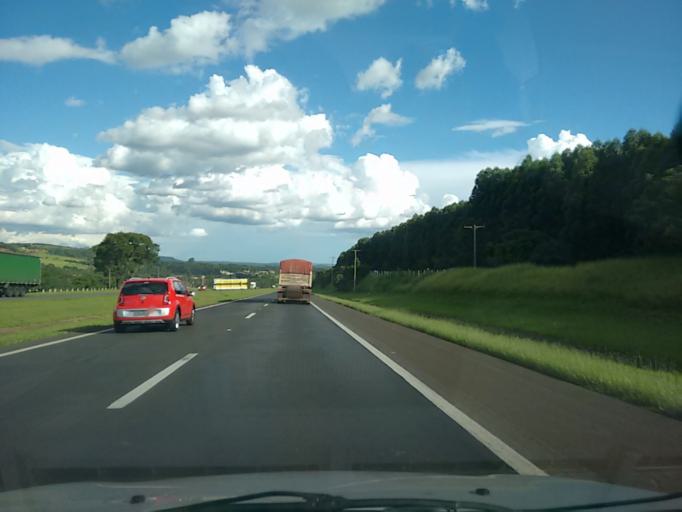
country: BR
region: Sao Paulo
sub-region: Sao Carlos
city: Sao Carlos
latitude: -22.0560
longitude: -47.8550
